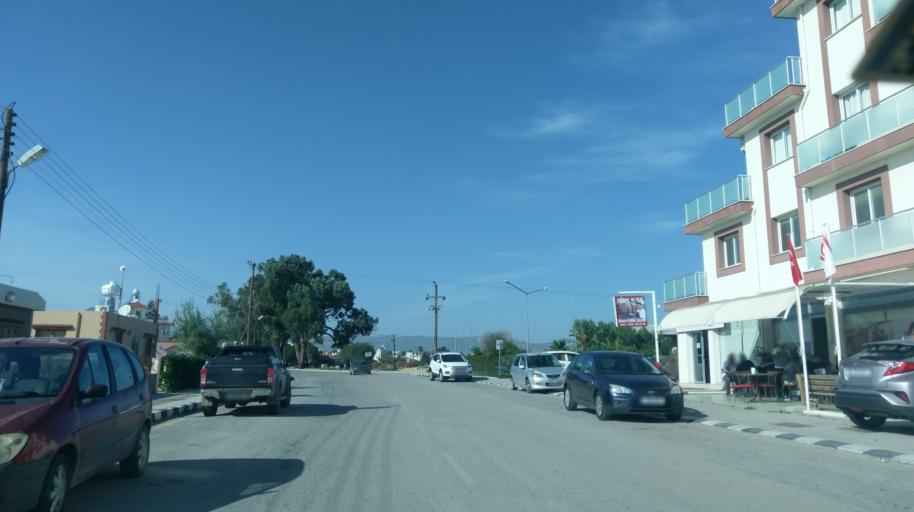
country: CY
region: Ammochostos
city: Trikomo
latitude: 35.2800
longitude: 33.8963
